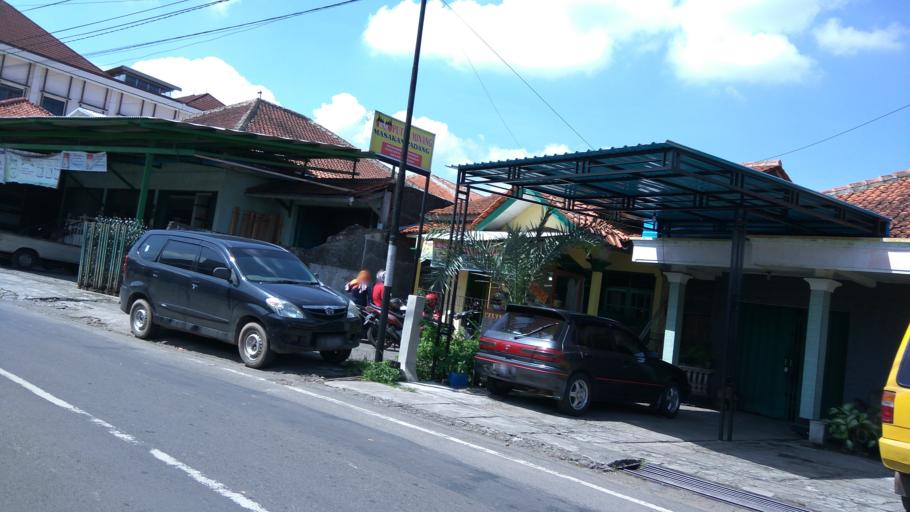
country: ID
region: Central Java
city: Ungaran
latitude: -7.1262
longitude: 110.4089
